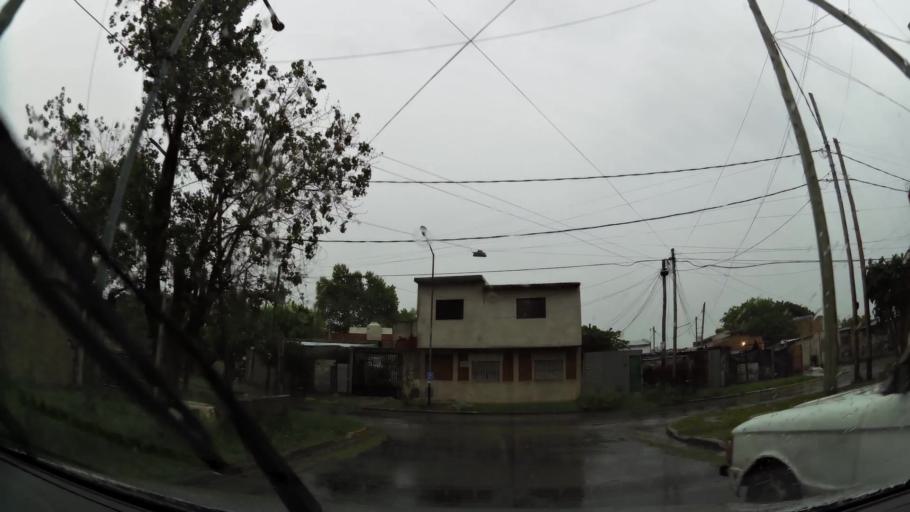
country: AR
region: Buenos Aires
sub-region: Partido de Lanus
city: Lanus
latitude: -34.7211
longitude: -58.4011
